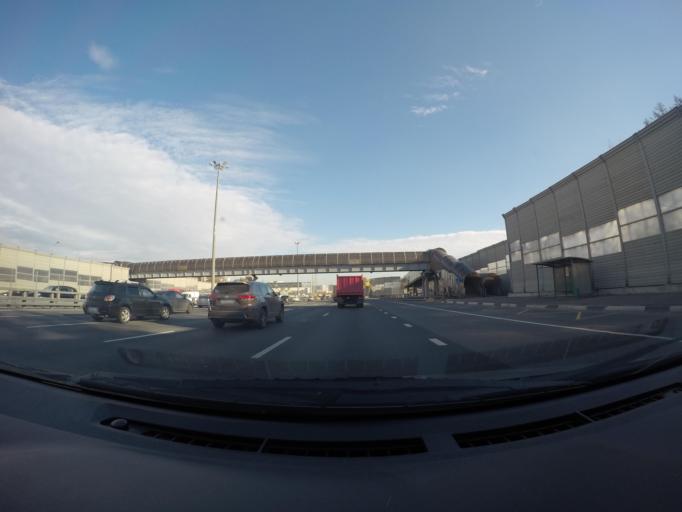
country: RU
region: Moskovskaya
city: Druzhba
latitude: 55.9016
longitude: 37.7580
